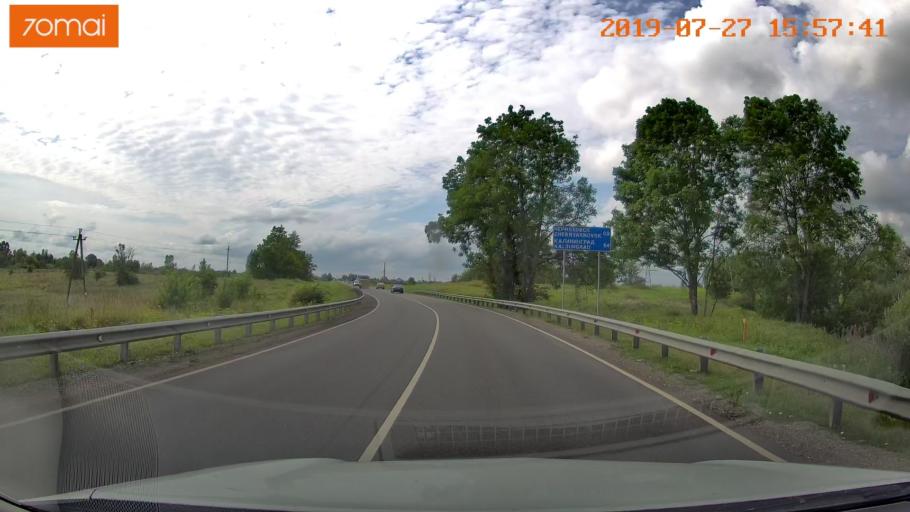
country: RU
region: Kaliningrad
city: Chernyakhovsk
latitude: 54.6248
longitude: 21.8793
